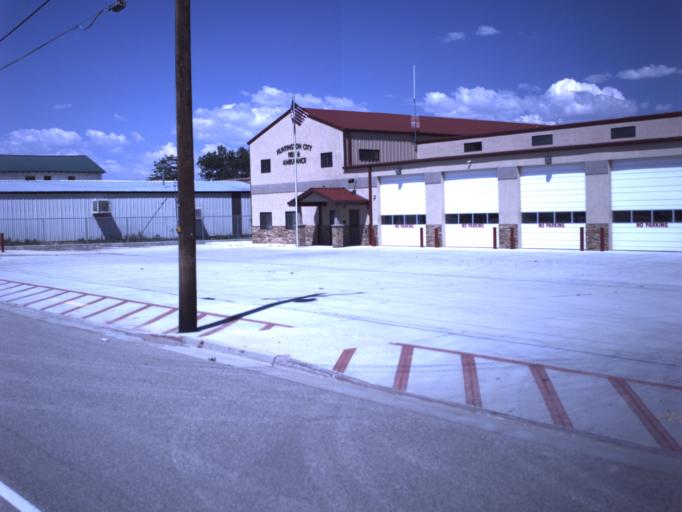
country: US
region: Utah
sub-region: Emery County
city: Huntington
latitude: 39.3325
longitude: -110.9646
